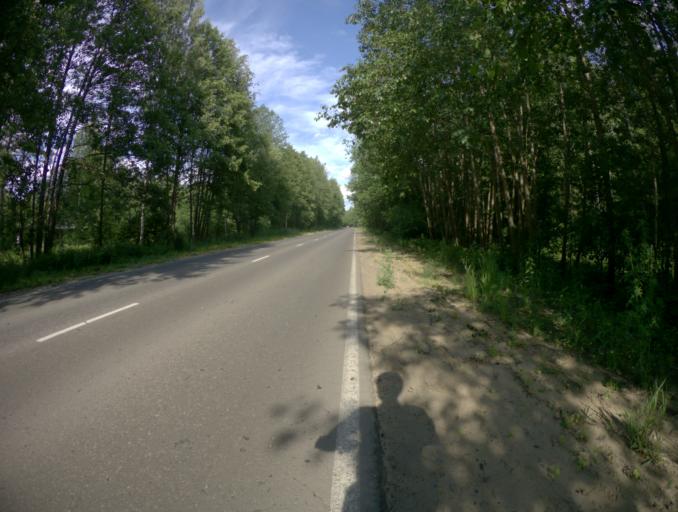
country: RU
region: Vladimir
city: Galitsy
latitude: 56.2875
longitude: 42.7995
